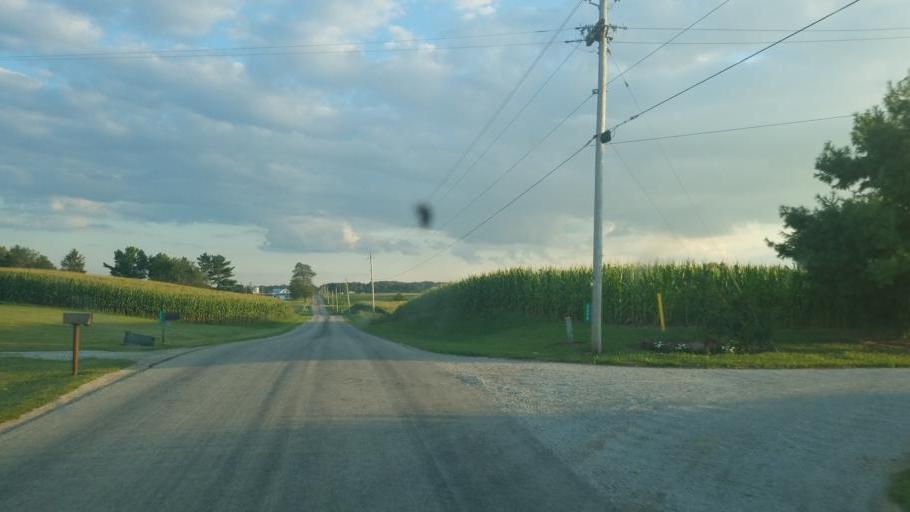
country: US
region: Ohio
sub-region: Richland County
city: Shelby
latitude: 40.9000
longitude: -82.5325
